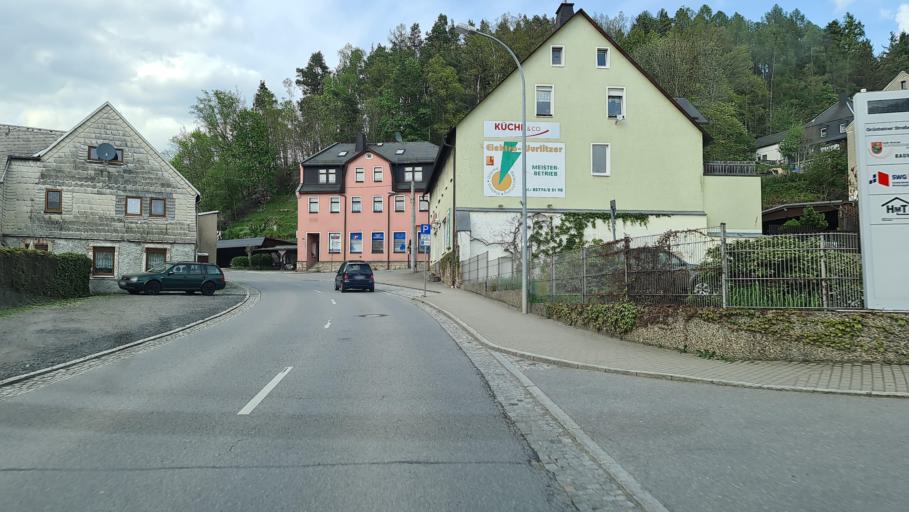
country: DE
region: Saxony
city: Schwarzenberg
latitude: 50.5496
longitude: 12.7817
